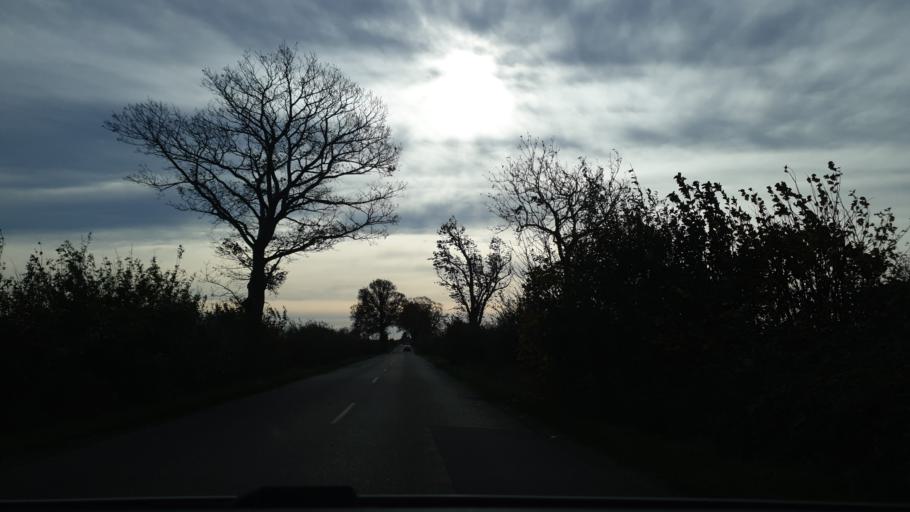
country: PL
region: Pomeranian Voivodeship
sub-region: Powiat pucki
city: Puck
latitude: 54.6921
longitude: 18.3658
